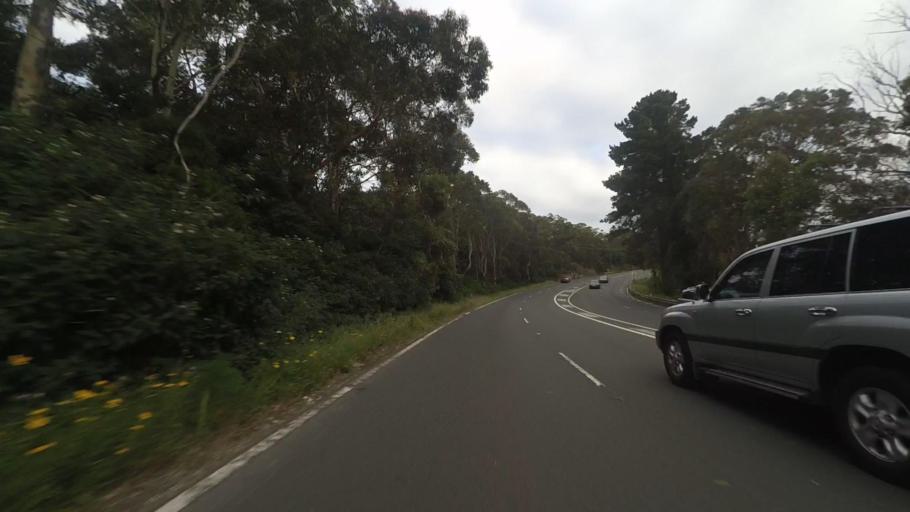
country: AU
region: New South Wales
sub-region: Sutherland Shire
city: Engadine
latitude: -34.0737
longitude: 151.0061
